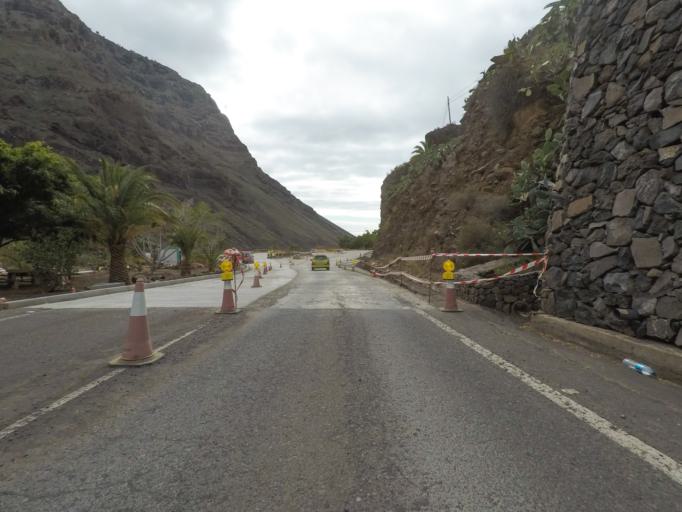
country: ES
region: Canary Islands
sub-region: Provincia de Santa Cruz de Tenerife
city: Alajero
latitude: 28.1033
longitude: -17.3283
